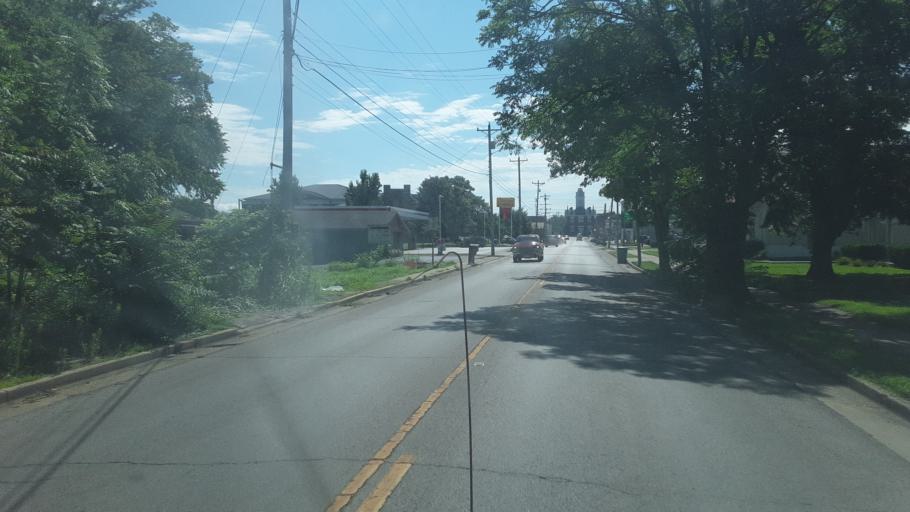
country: US
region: Kentucky
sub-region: Todd County
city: Elkton
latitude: 36.8104
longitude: -87.1581
